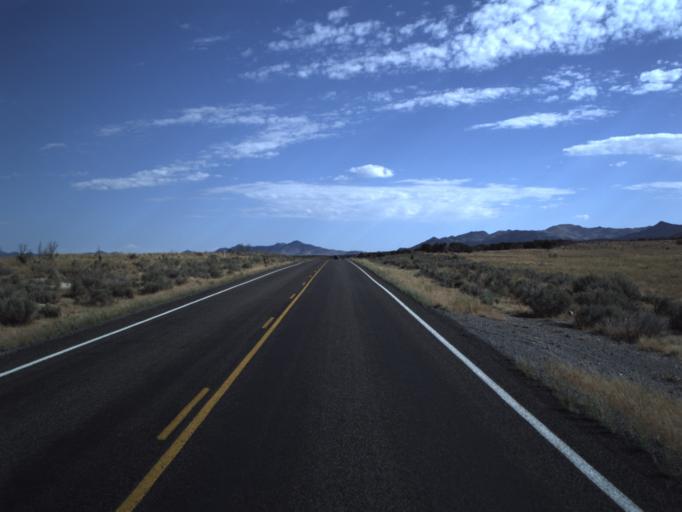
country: US
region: Utah
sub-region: Juab County
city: Mona
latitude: 39.7352
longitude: -112.1915
